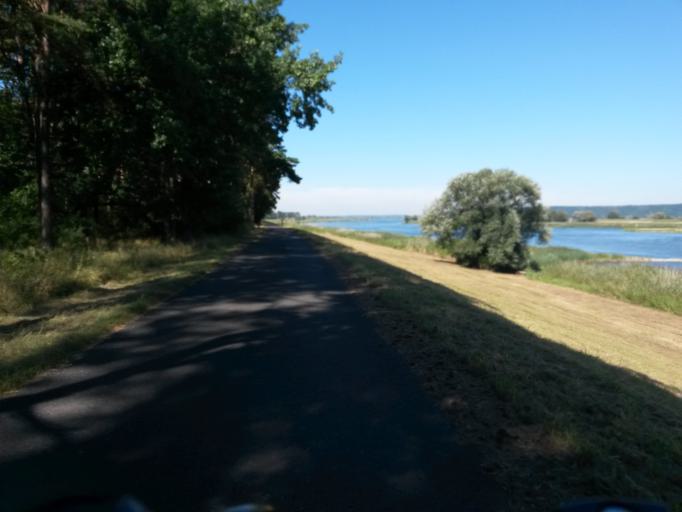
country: PL
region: West Pomeranian Voivodeship
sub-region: Powiat gryfinski
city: Cedynia
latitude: 52.8909
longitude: 14.1569
